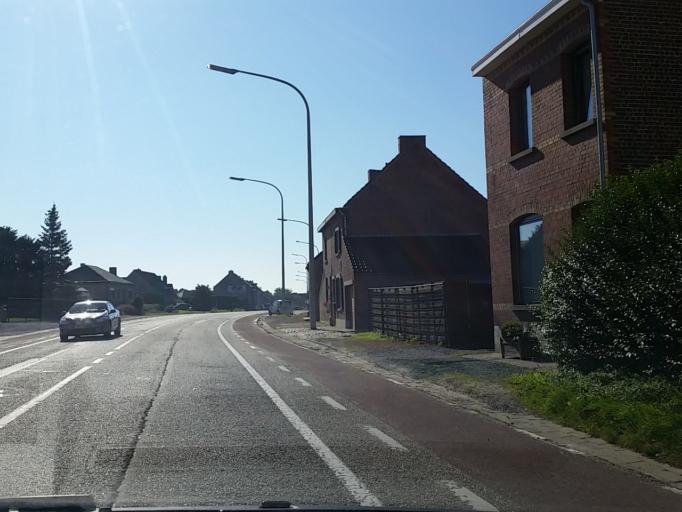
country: BE
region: Flanders
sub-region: Provincie Vlaams-Brabant
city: Zemst
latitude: 50.9679
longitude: 4.4555
